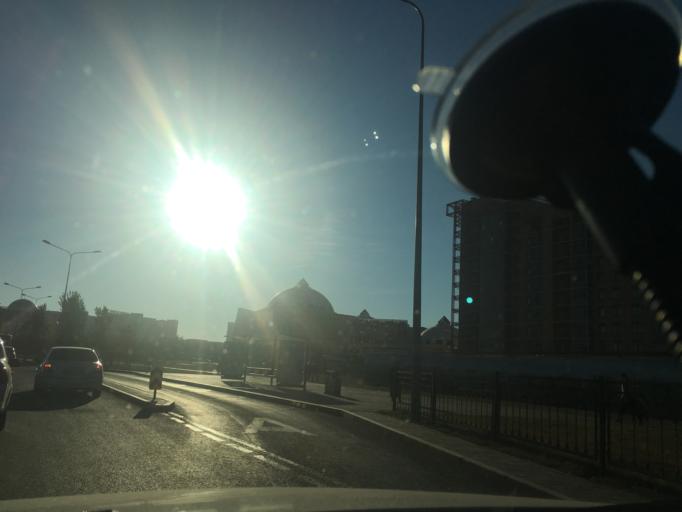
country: KZ
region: Astana Qalasy
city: Astana
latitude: 51.1458
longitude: 71.4071
